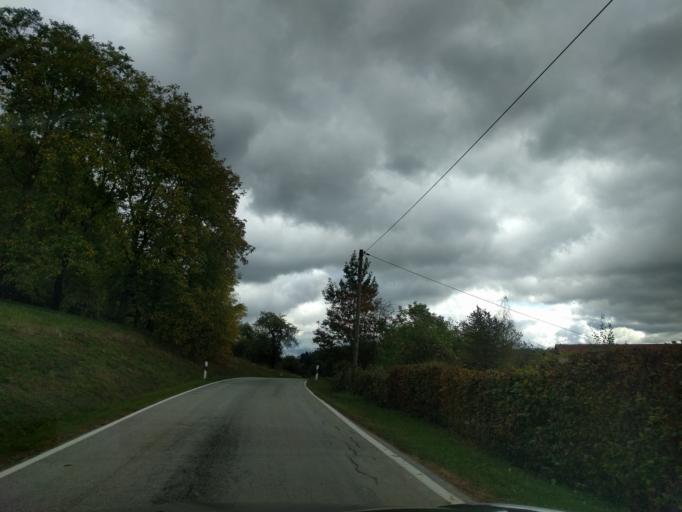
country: DE
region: Bavaria
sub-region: Lower Bavaria
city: Schaufling
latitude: 48.8346
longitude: 13.0917
